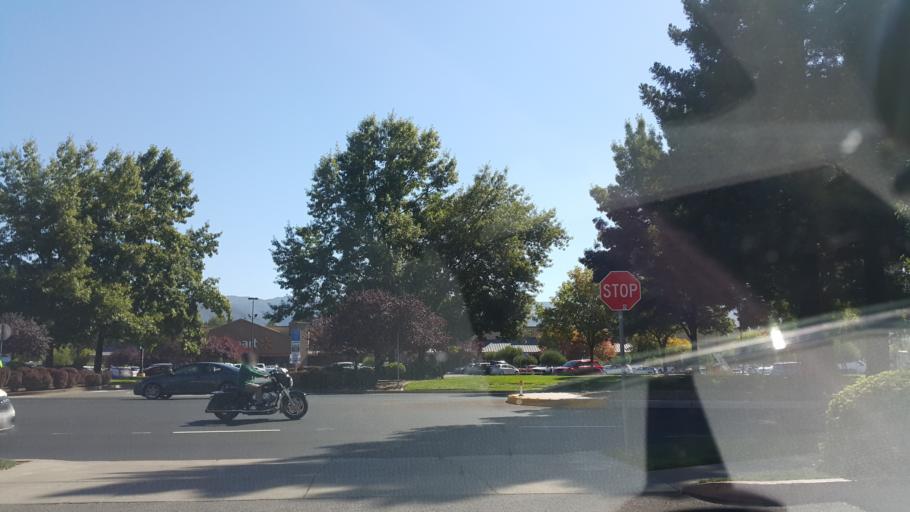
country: US
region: California
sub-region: Mendocino County
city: Ukiah
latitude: 39.1338
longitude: -123.1992
